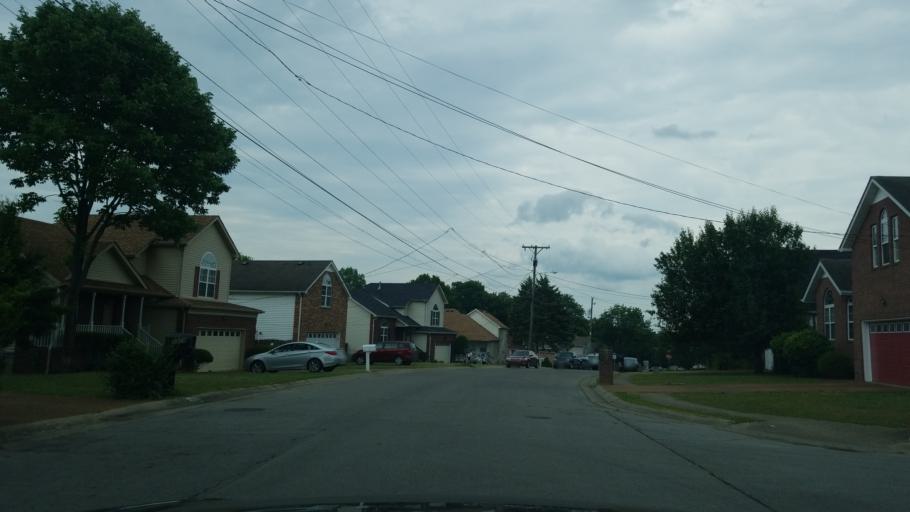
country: US
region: Tennessee
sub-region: Rutherford County
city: La Vergne
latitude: 36.0833
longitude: -86.5838
